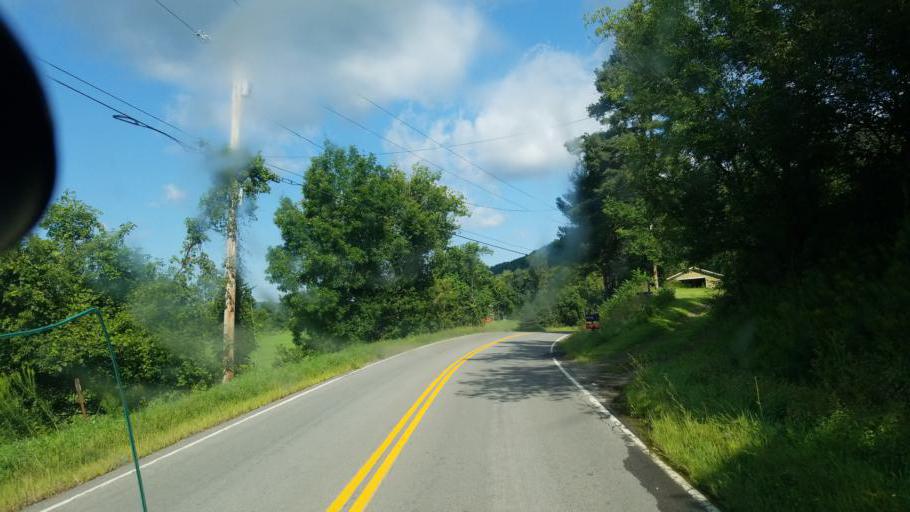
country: US
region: New York
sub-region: Steuben County
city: Canisteo
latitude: 42.2887
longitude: -77.6130
